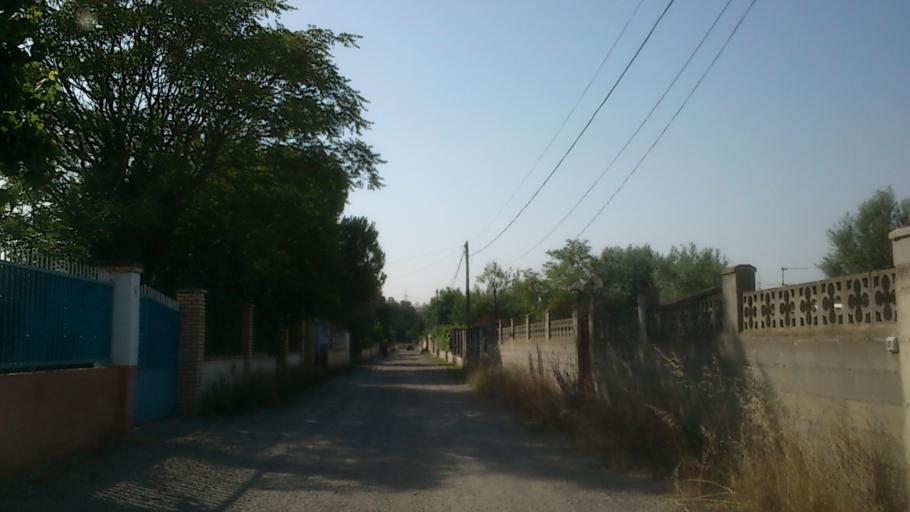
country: ES
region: Aragon
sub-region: Provincia de Zaragoza
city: Villanueva de Gallego
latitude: 41.7618
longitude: -0.8033
